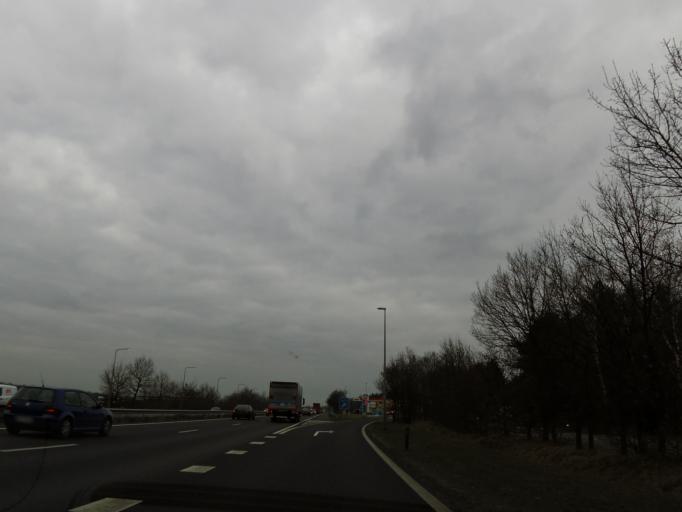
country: NL
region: North Brabant
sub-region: Gemeente Cranendonck
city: Cranendonck
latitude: 51.3234
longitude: 5.5935
